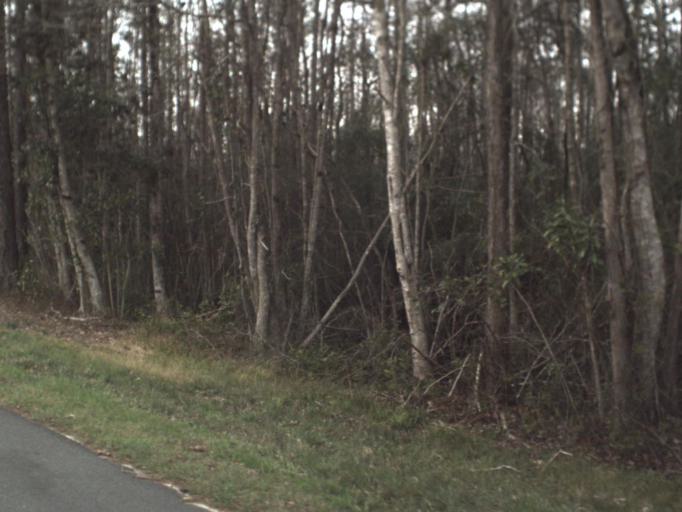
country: US
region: Florida
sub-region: Gulf County
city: Wewahitchka
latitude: 30.1349
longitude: -85.2394
